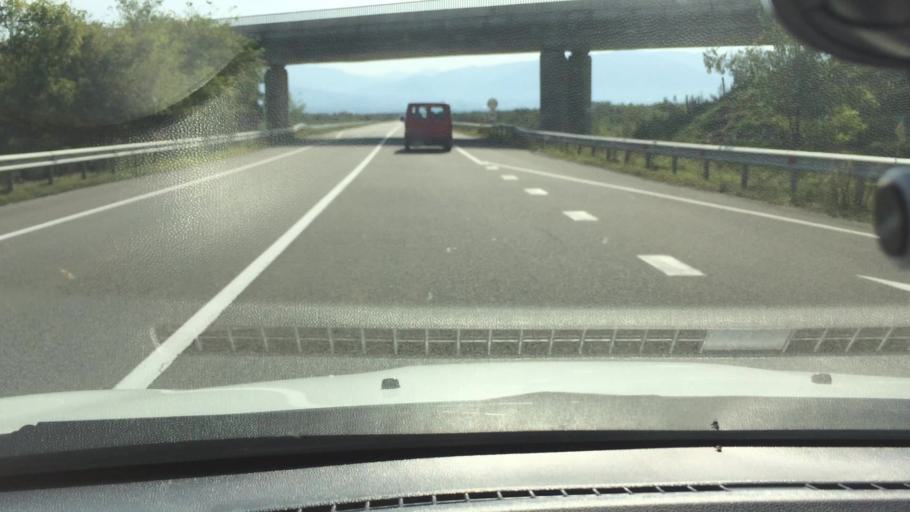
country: GE
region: Ajaria
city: Ochkhamuri
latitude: 41.8991
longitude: 41.7965
